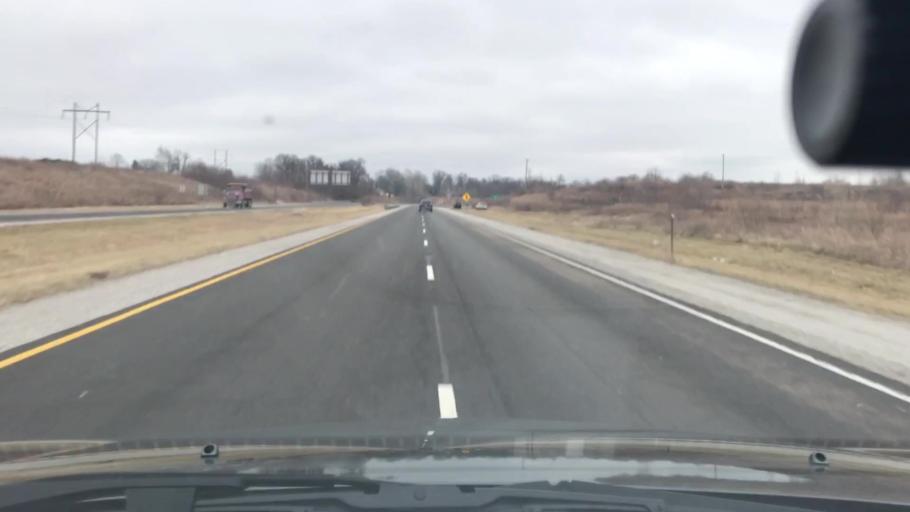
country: US
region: Illinois
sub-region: Madison County
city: Roxana
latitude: 38.8690
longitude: -90.0581
